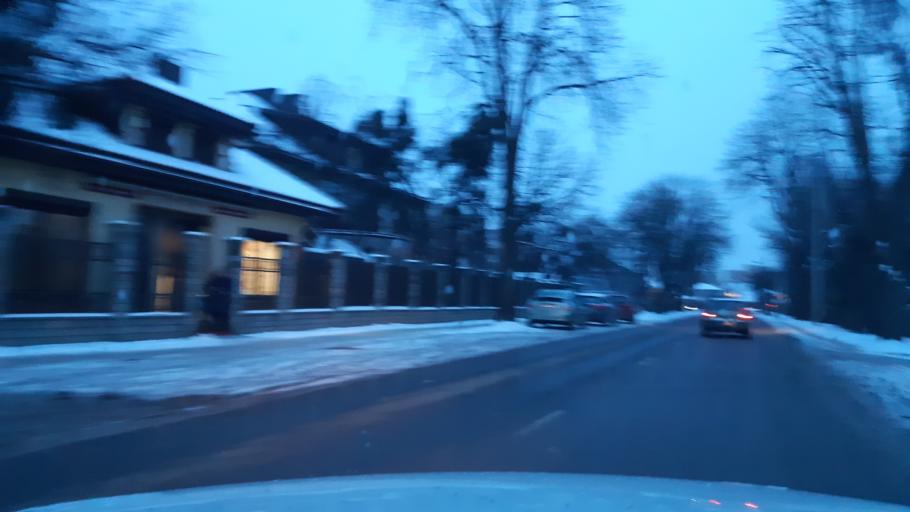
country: LT
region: Kauno apskritis
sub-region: Kaunas
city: Eiguliai
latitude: 54.9130
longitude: 23.9405
